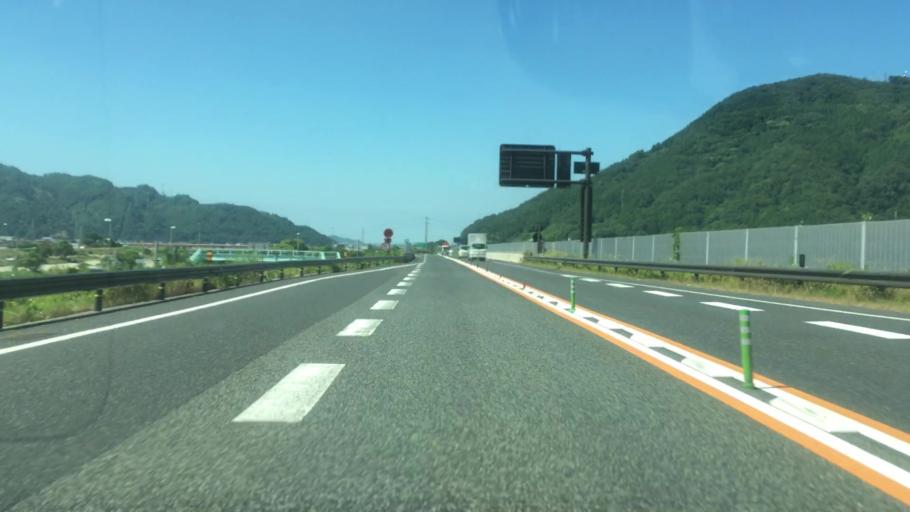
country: JP
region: Tottori
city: Tottori
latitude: 35.3988
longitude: 134.2049
